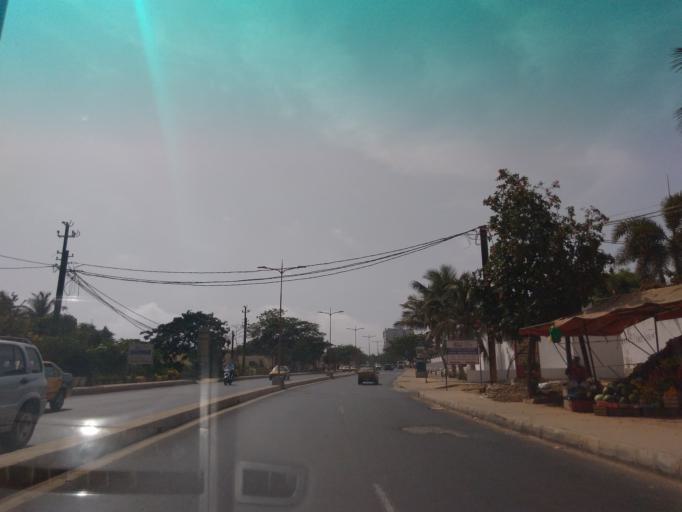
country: SN
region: Dakar
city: Mermoz Boabab
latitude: 14.7045
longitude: -17.4775
